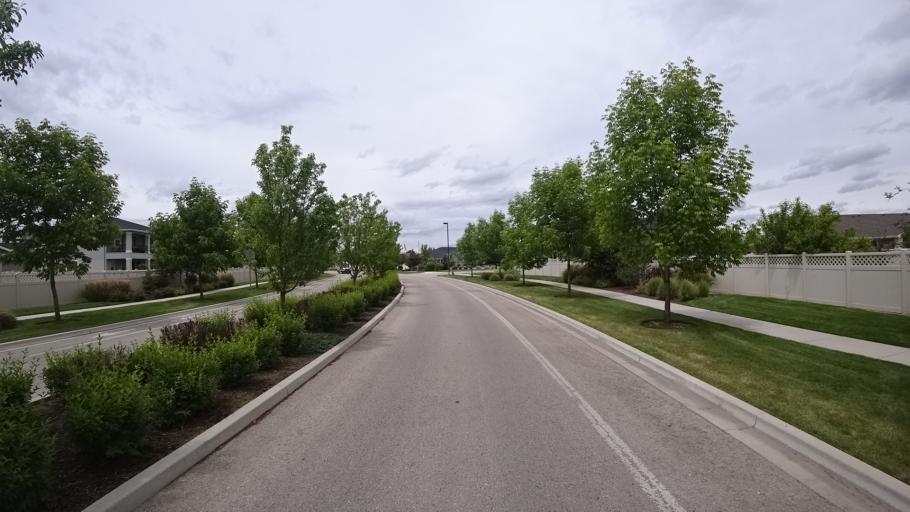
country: US
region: Idaho
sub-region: Ada County
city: Meridian
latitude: 43.6390
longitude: -116.4302
